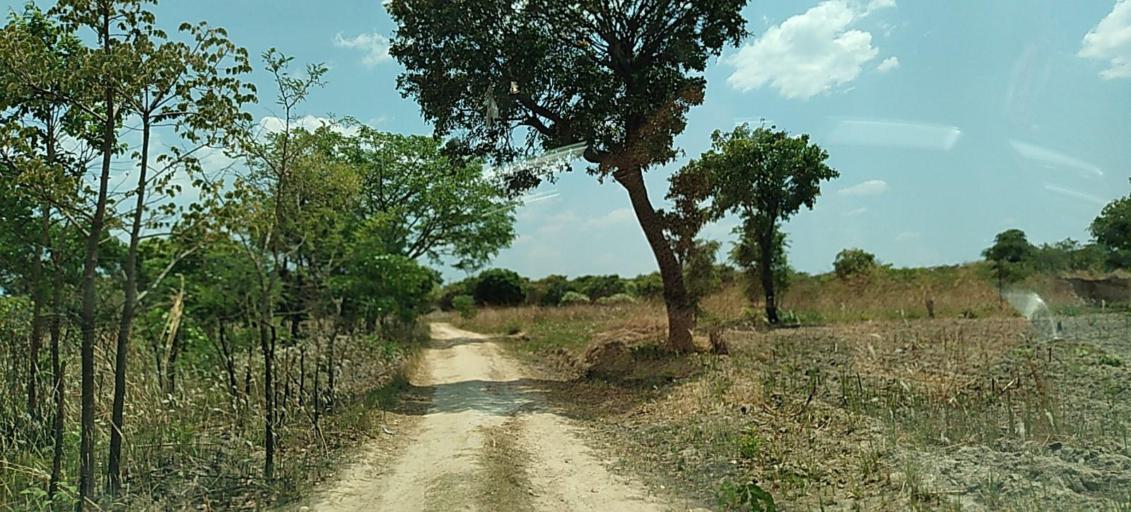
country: ZM
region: Copperbelt
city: Chililabombwe
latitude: -12.4767
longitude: 27.6656
